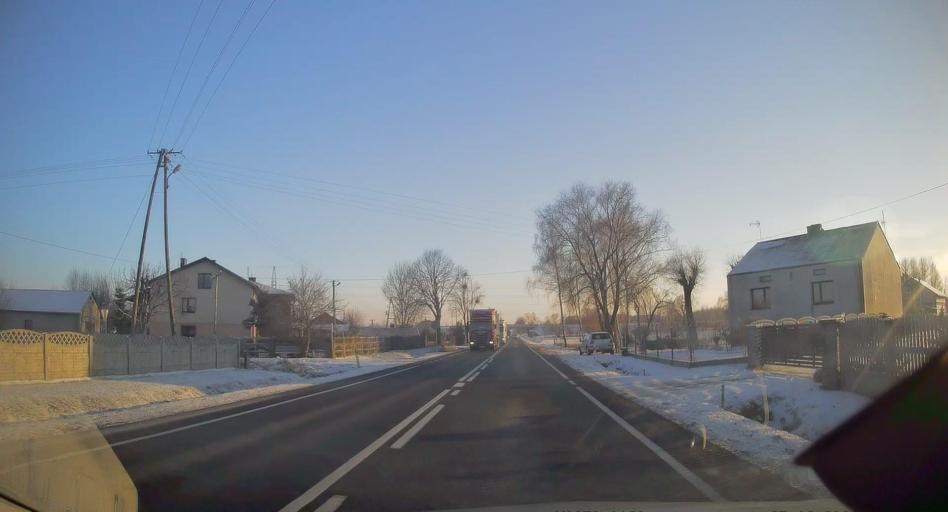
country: PL
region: Lodz Voivodeship
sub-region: Powiat opoczynski
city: Paradyz
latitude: 51.2830
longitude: 20.1463
